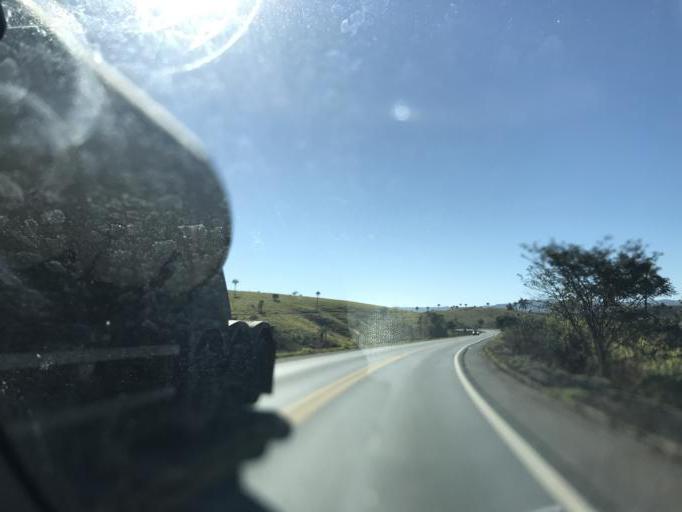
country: BR
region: Minas Gerais
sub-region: Bambui
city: Bambui
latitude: -19.8376
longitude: -46.0023
